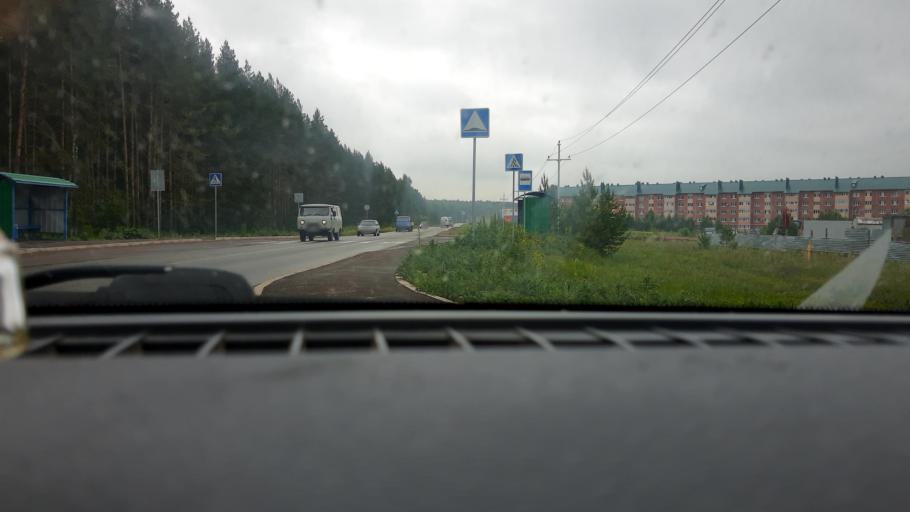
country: RU
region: Bashkortostan
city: Belebey
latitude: 54.0880
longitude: 54.0934
